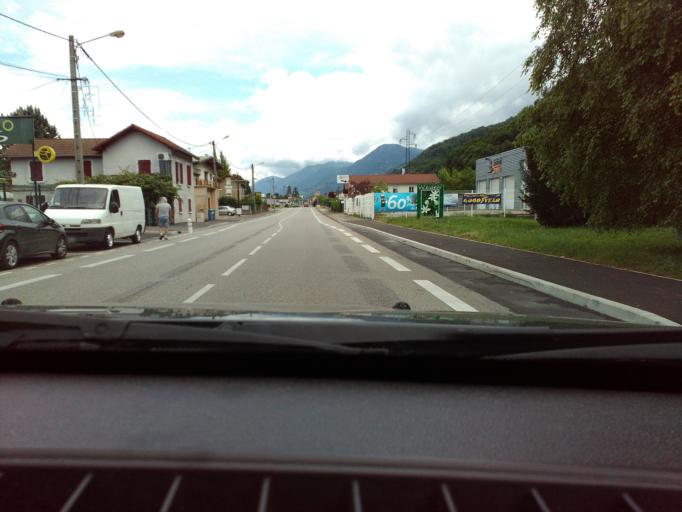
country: FR
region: Rhone-Alpes
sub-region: Departement de l'Isere
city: Froges
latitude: 45.2670
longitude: 5.9177
